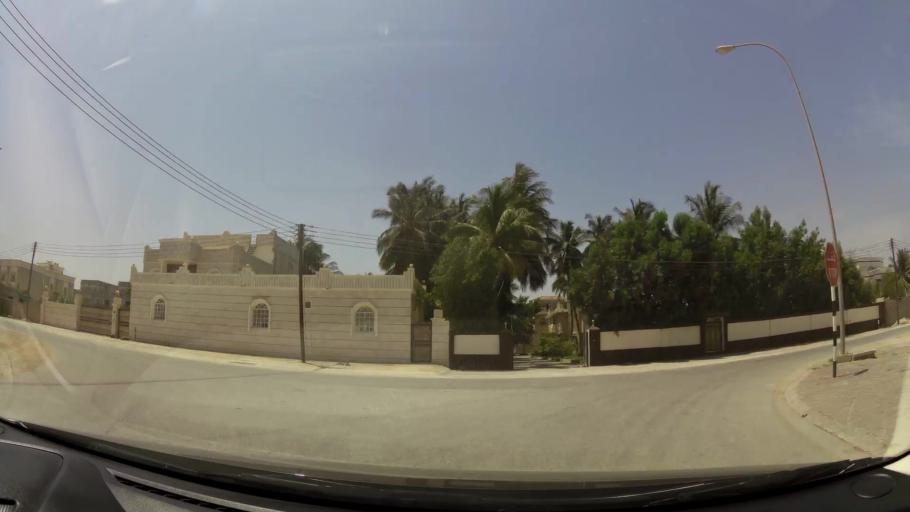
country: OM
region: Zufar
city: Salalah
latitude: 17.0579
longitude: 54.1579
